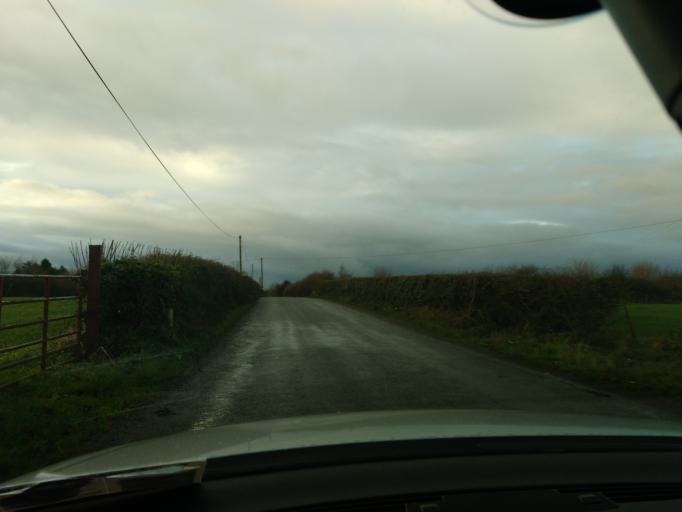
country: IE
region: Munster
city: Thurles
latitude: 52.6331
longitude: -7.8035
